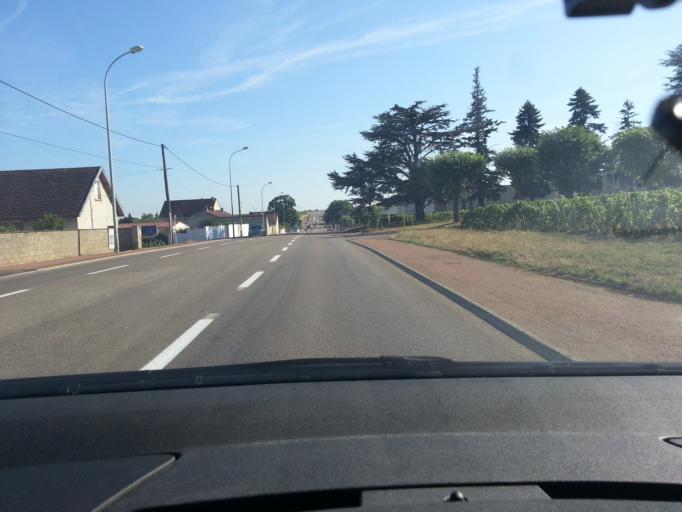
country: FR
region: Bourgogne
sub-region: Departement de la Cote-d'Or
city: Nuits-Saint-Georges
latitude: 47.1572
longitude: 4.9597
